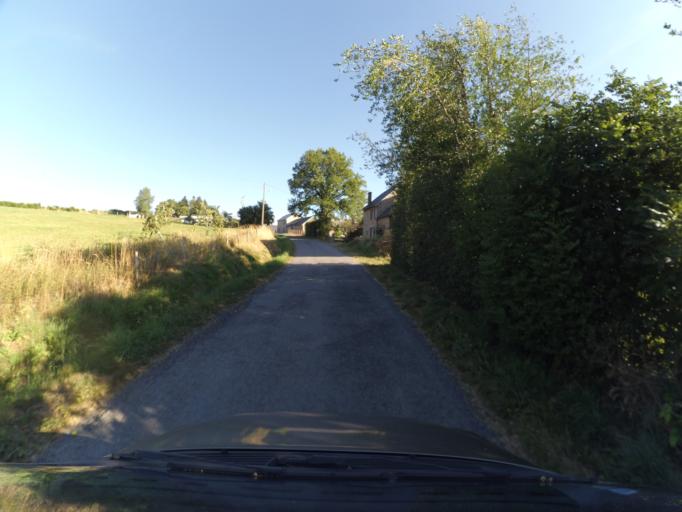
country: FR
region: Limousin
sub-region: Departement de la Creuse
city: Banize
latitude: 45.7365
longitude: 2.0382
